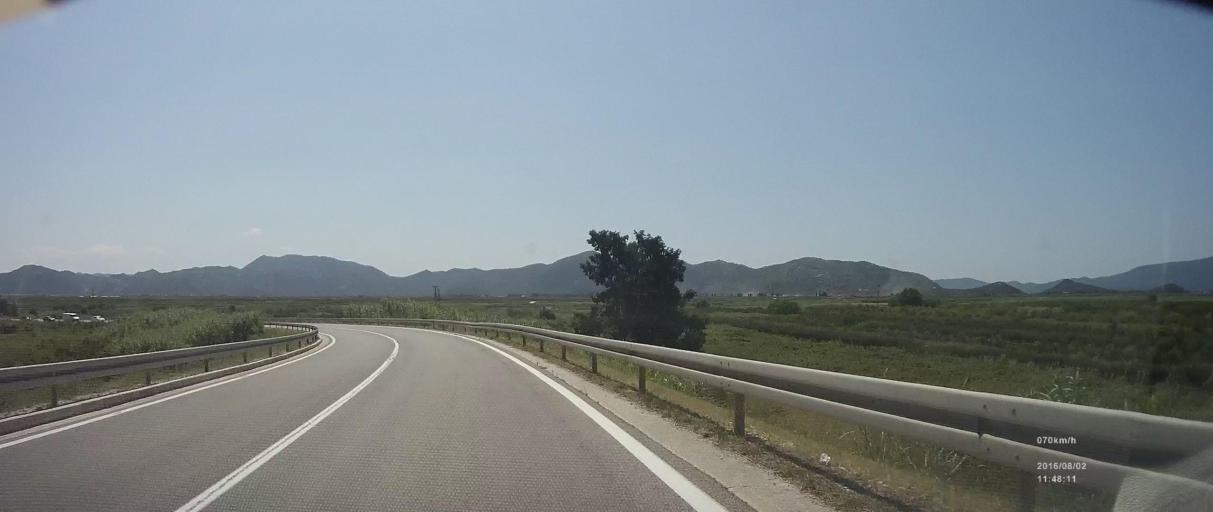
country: HR
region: Dubrovacko-Neretvanska
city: Komin
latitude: 43.0357
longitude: 17.4864
